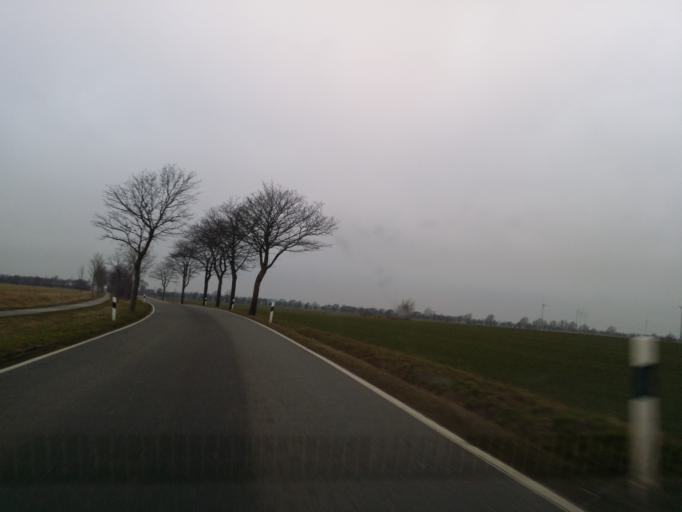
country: DE
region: Schleswig-Holstein
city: Fehmarn
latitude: 54.4649
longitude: 11.1158
